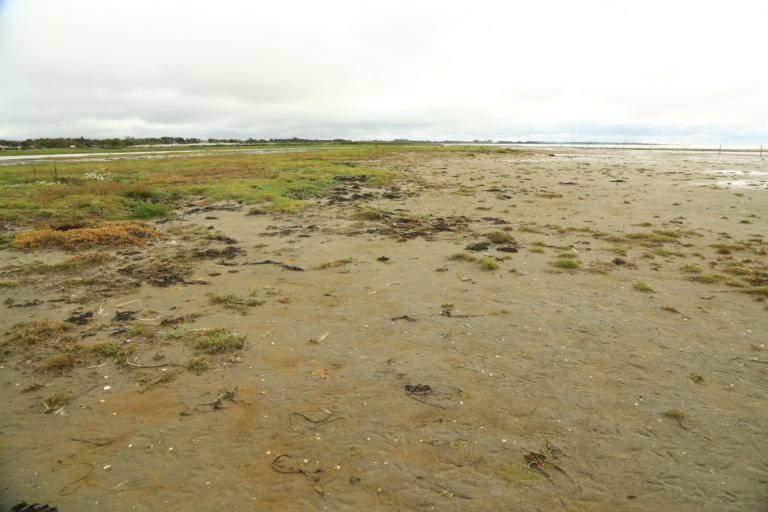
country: SE
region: Halland
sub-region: Varbergs Kommun
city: Tvaaker
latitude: 57.0136
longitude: 12.3404
